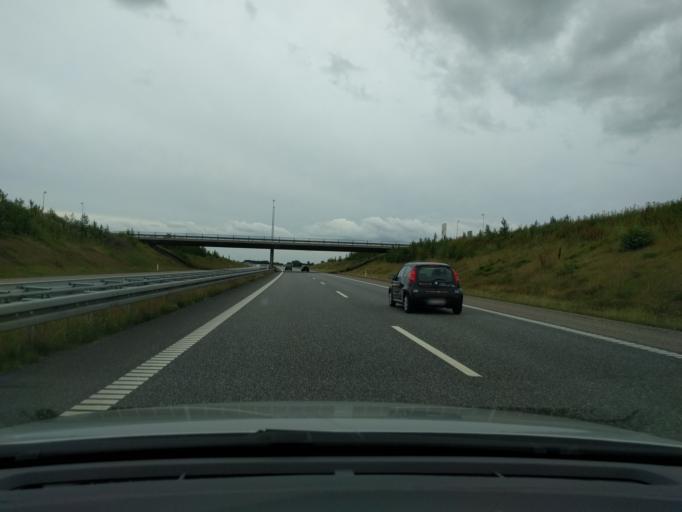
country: DK
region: Central Jutland
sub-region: Hedensted Kommune
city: Torring
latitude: 55.8020
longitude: 9.5638
